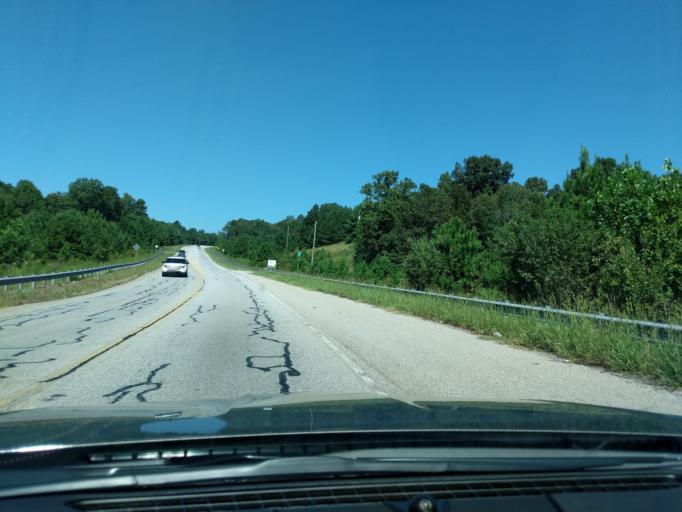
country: US
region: Georgia
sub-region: Habersham County
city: Demorest
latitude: 34.5737
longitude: -83.5905
